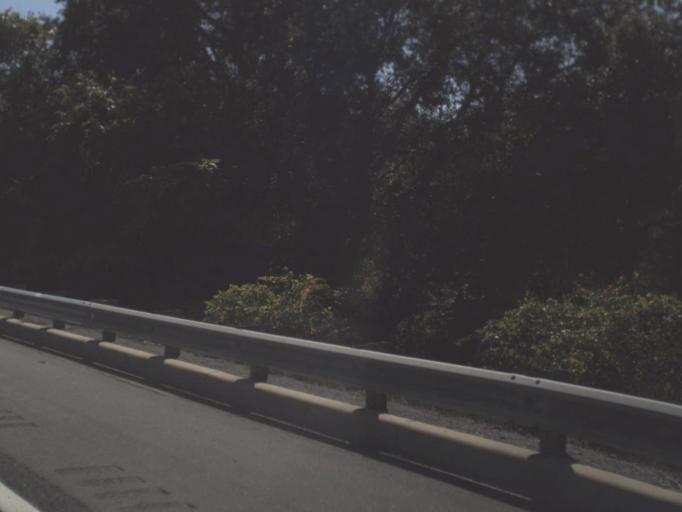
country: US
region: Florida
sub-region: Lake County
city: Hawthorne
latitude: 28.7297
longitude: -81.9119
